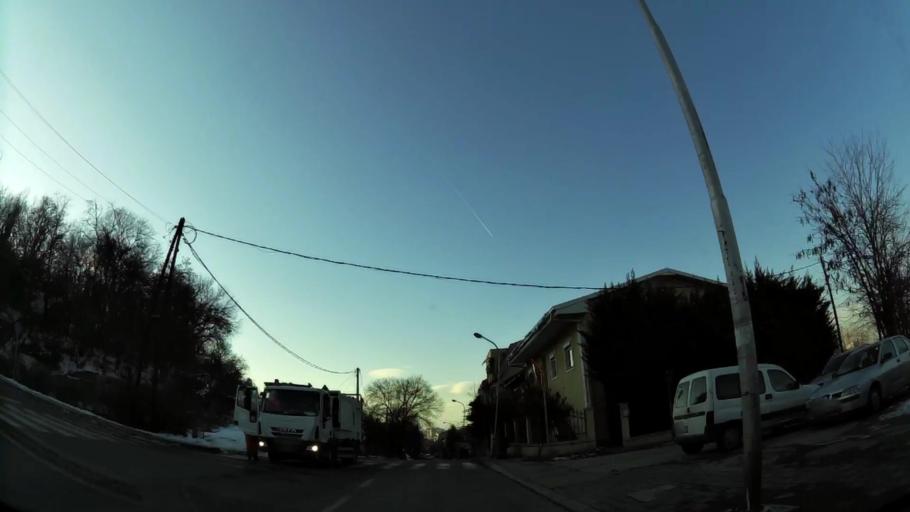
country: MK
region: Karpos
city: Skopje
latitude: 41.9954
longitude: 21.3936
